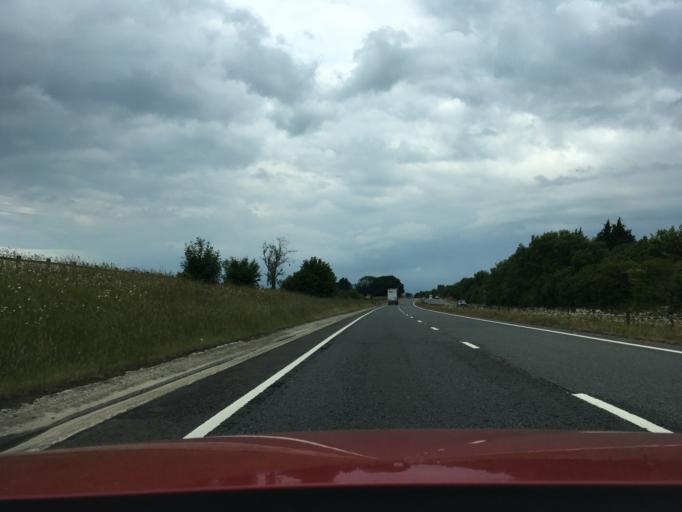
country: GB
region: England
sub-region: Gloucestershire
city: Coates
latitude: 51.7907
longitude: -2.0455
